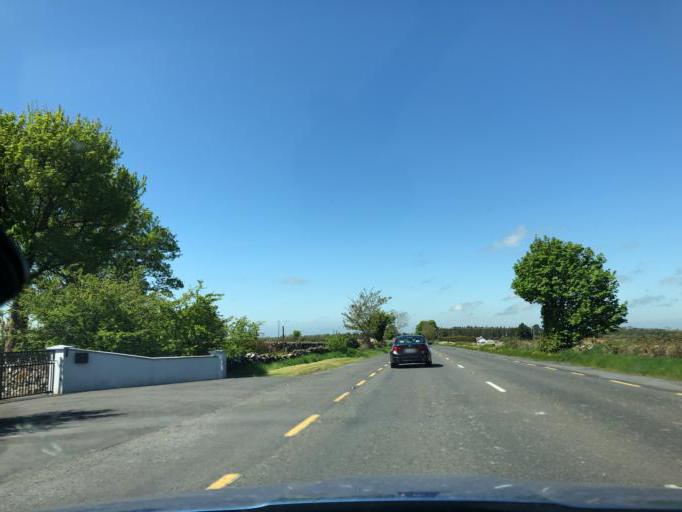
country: IE
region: Connaught
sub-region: County Galway
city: Loughrea
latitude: 53.2062
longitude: -8.6089
